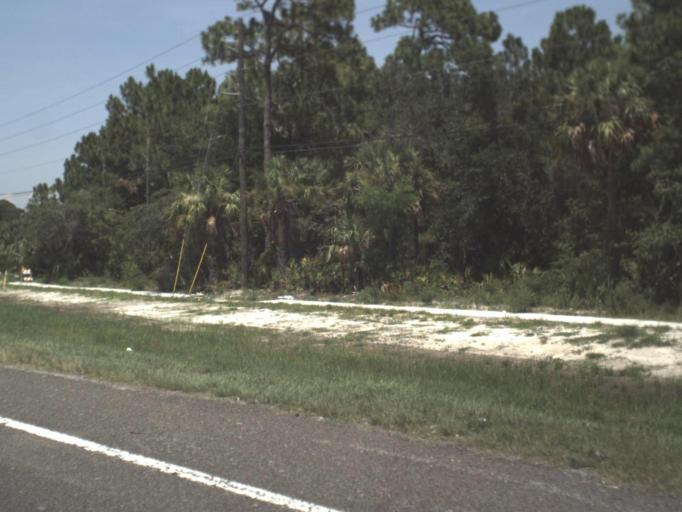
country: US
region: Florida
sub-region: Pasco County
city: Hudson
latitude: 28.3561
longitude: -82.6984
